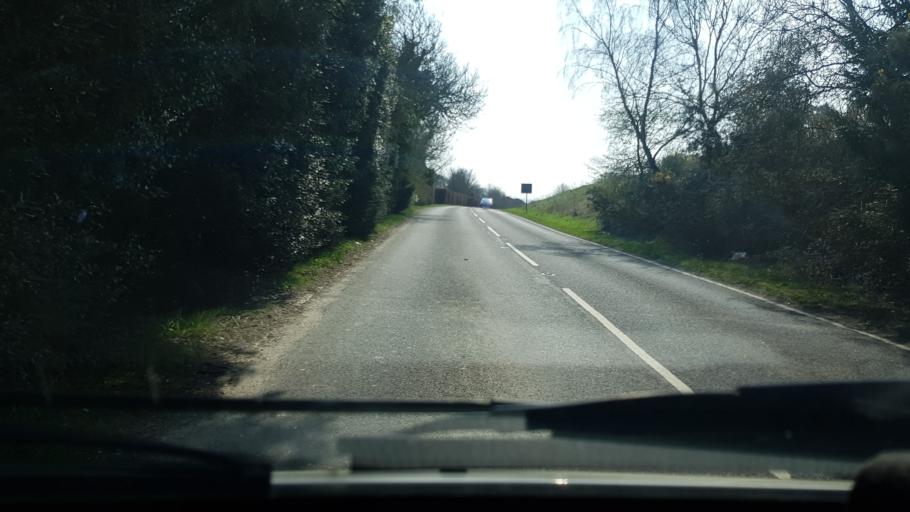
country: GB
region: England
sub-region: West Sussex
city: Boxgrove
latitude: 50.8941
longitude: -0.7494
